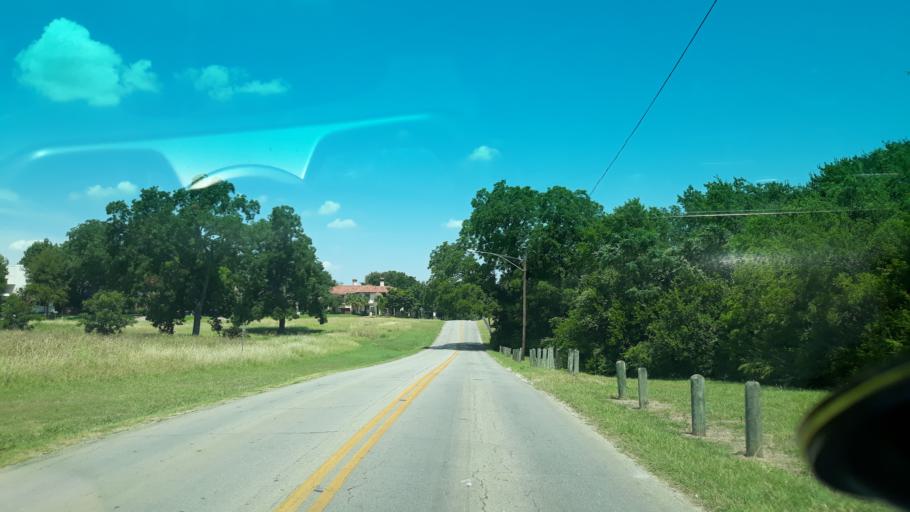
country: US
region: Texas
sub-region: Dallas County
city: Highland Park
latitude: 32.8217
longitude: -96.7314
